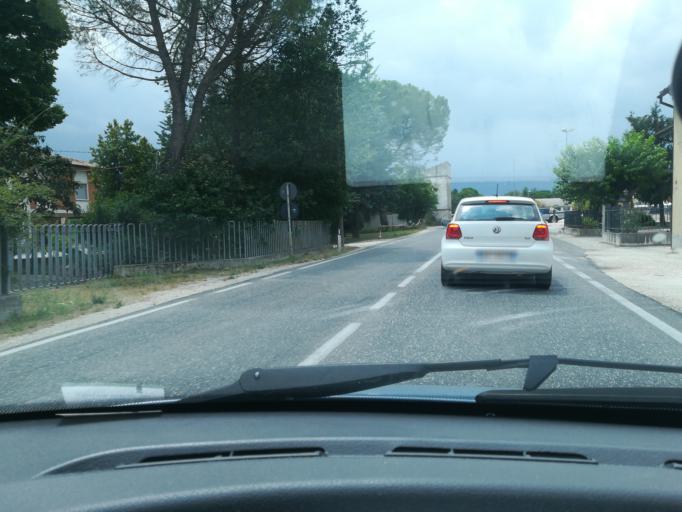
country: IT
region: The Marches
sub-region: Provincia di Macerata
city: Montecassiano
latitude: 43.3514
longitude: 13.4689
